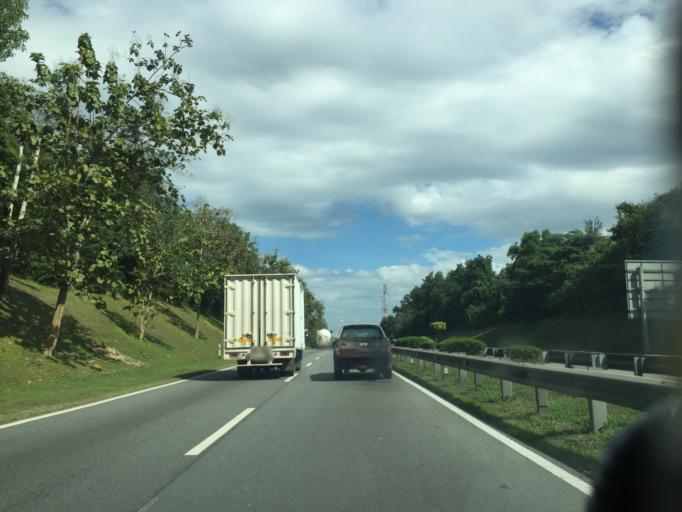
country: MY
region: Kedah
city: Jitra
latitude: 6.3260
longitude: 100.4204
